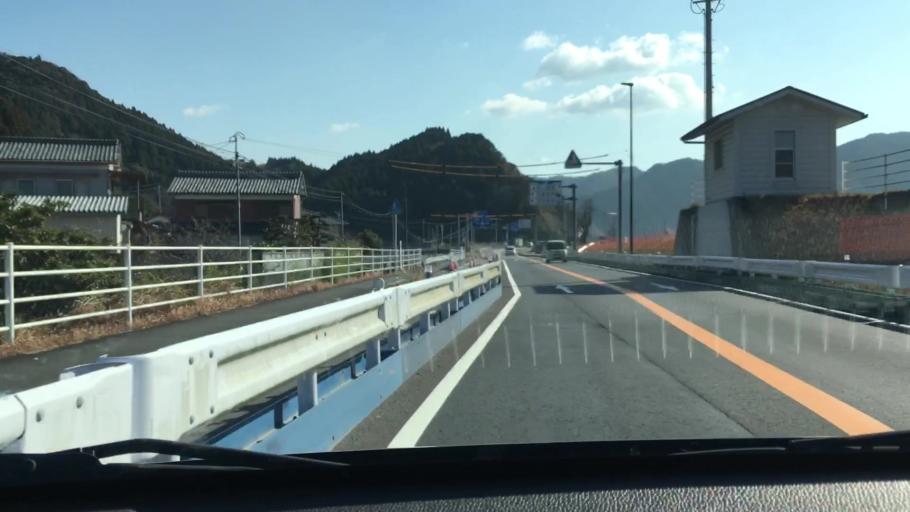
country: JP
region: Oita
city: Saiki
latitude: 32.9593
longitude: 131.8426
